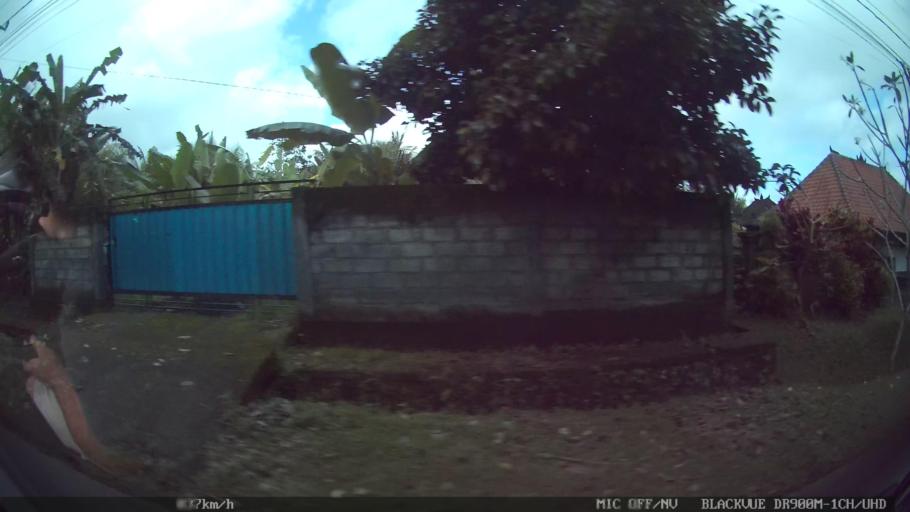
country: ID
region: Bali
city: Banjar Pesalakan
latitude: -8.4900
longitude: 115.3045
